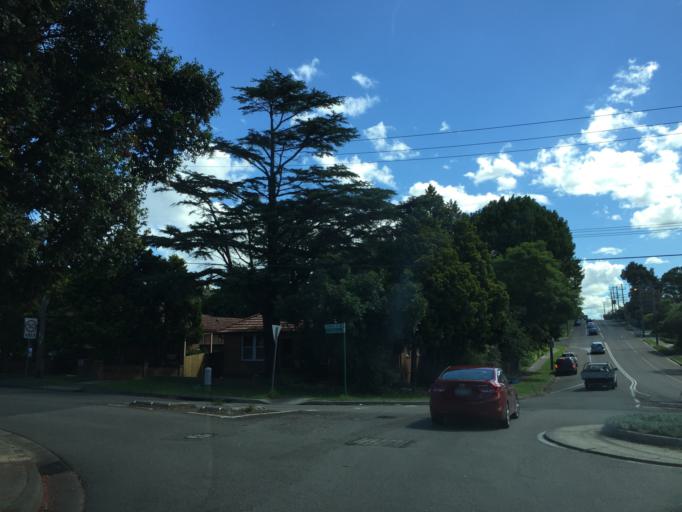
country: AU
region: New South Wales
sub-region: Ryde
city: Marsfield
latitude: -33.7812
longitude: 151.1004
